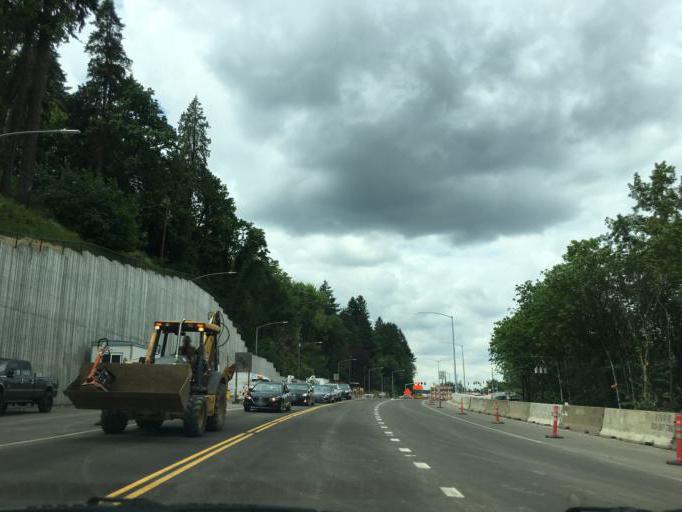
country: US
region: Oregon
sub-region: Clackamas County
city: Milwaukie
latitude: 45.4616
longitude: -122.6681
